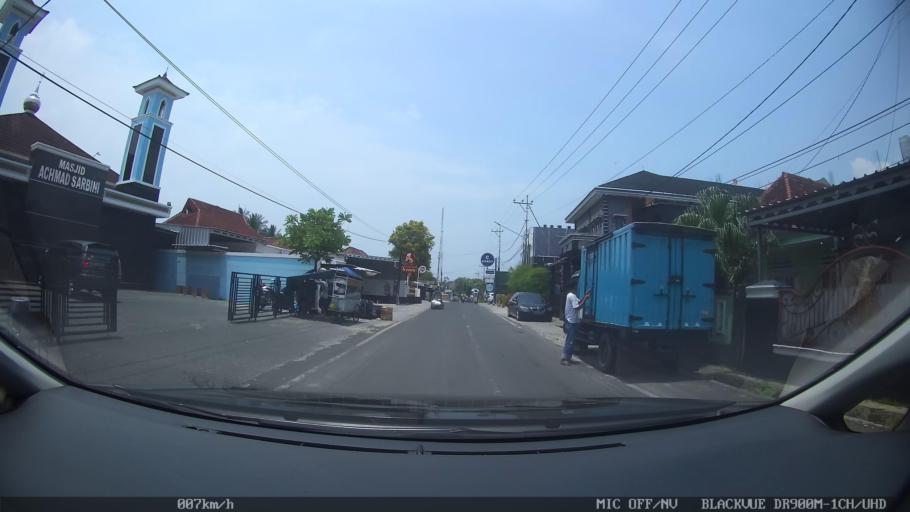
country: ID
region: Lampung
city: Bandarlampung
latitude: -5.4181
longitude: 105.2624
